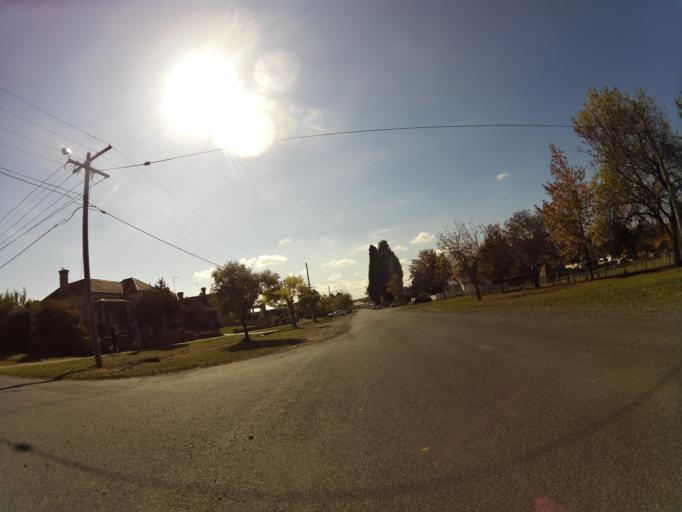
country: AU
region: Victoria
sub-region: Ballarat North
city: Lake Wendouree
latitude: -37.5468
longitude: 143.8479
